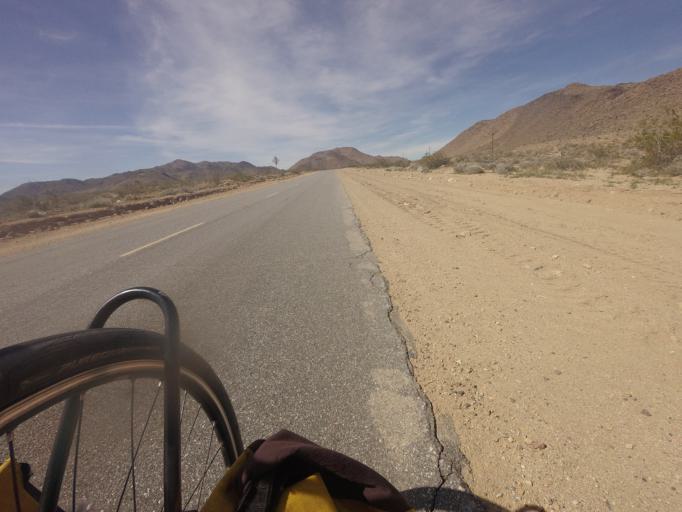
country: US
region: California
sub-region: San Bernardino County
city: Searles Valley
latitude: 35.5752
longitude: -117.4515
